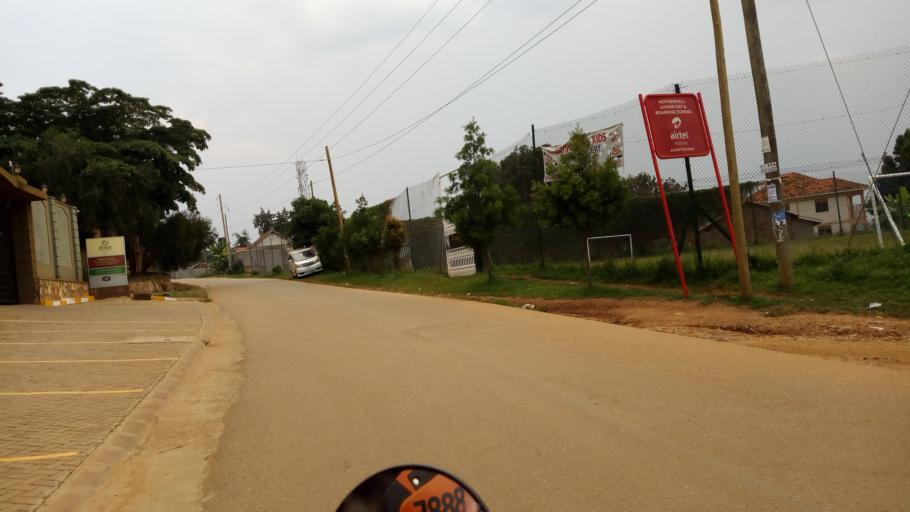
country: UG
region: Central Region
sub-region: Wakiso District
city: Kireka
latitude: 0.3188
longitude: 32.6433
